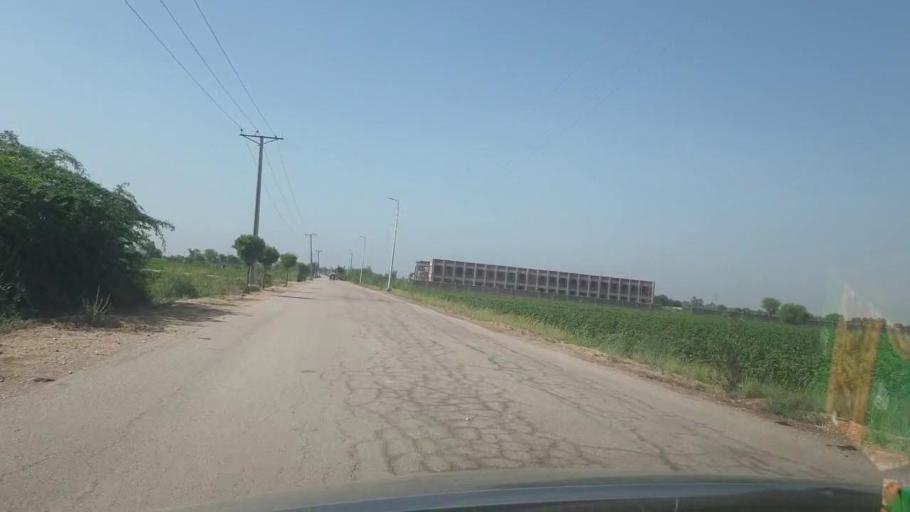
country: PK
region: Sindh
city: Rohri
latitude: 27.5173
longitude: 69.0359
